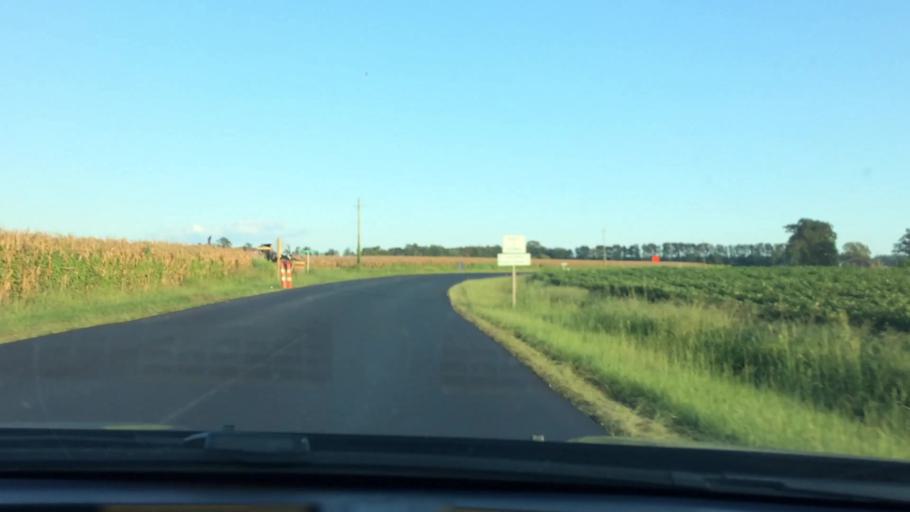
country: US
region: North Carolina
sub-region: Pitt County
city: Ayden
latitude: 35.4428
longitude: -77.4545
